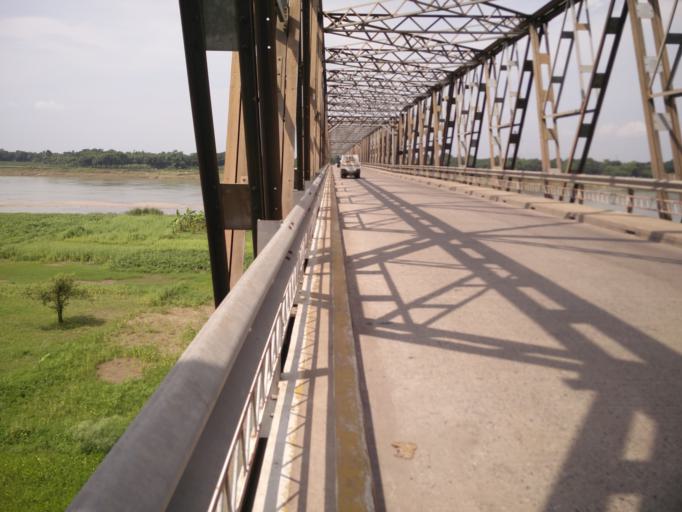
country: BD
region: Khulna
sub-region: Magura
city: Magura
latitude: 23.5440
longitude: 89.5180
